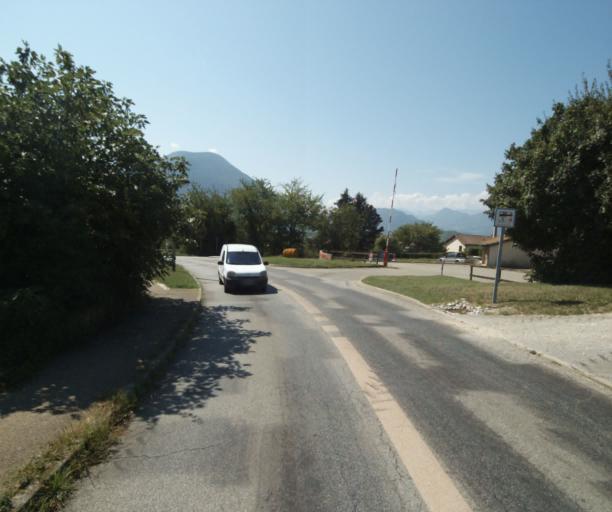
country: FR
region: Rhone-Alpes
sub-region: Departement de l'Isere
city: Champagnier
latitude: 45.1016
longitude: 5.7419
